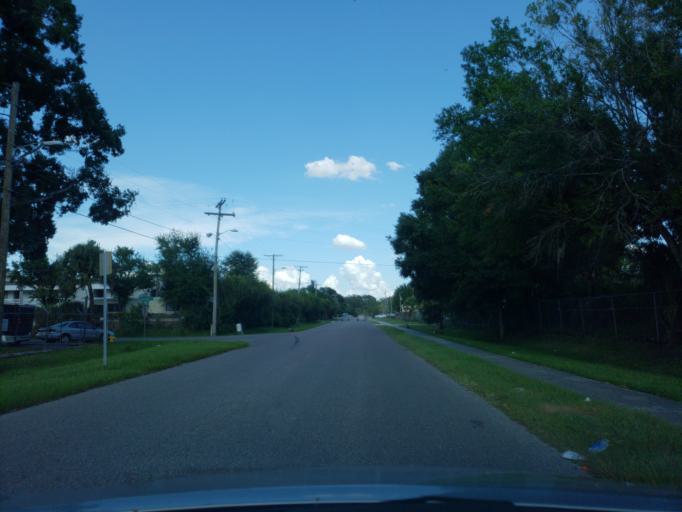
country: US
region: Florida
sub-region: Hillsborough County
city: Egypt Lake-Leto
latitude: 27.9864
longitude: -82.5085
